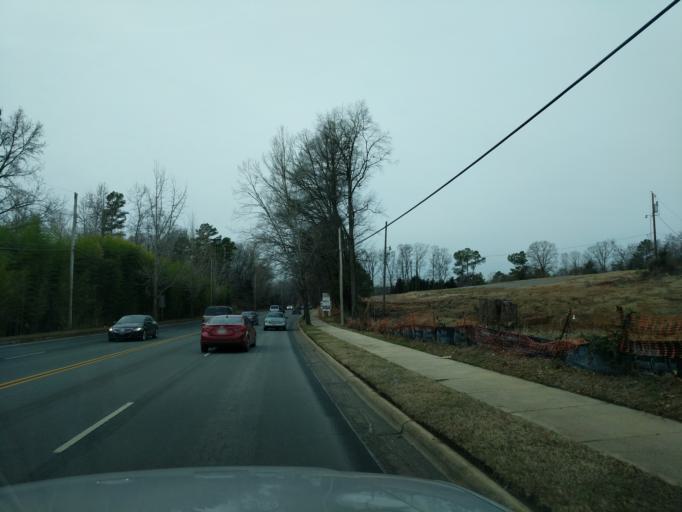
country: US
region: North Carolina
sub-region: Mecklenburg County
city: Charlotte
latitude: 35.1893
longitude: -80.8017
